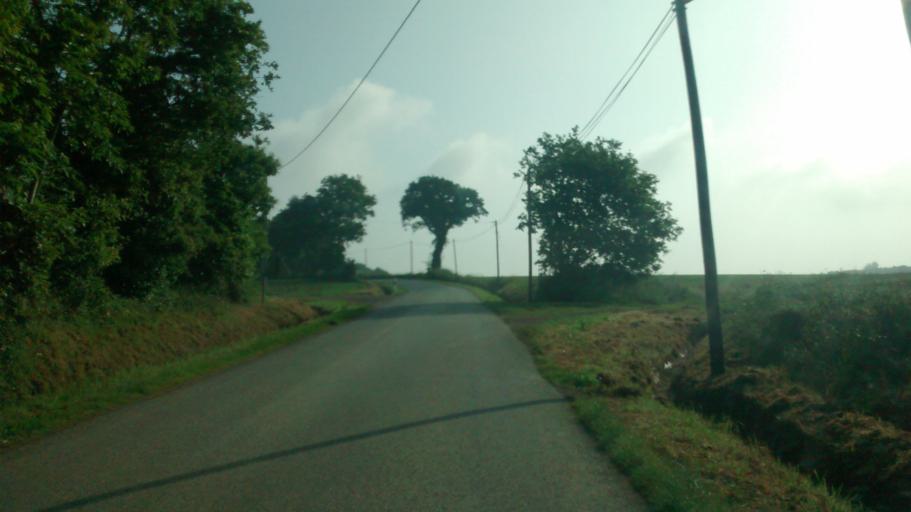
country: FR
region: Brittany
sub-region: Departement du Morbihan
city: Ruffiac
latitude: 47.8284
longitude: -2.2812
